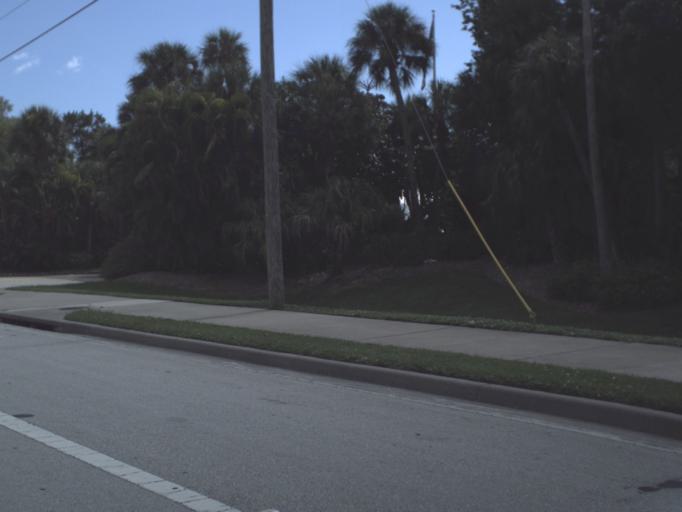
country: US
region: Florida
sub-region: Sarasota County
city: Nokomis
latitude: 27.1114
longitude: -82.4464
